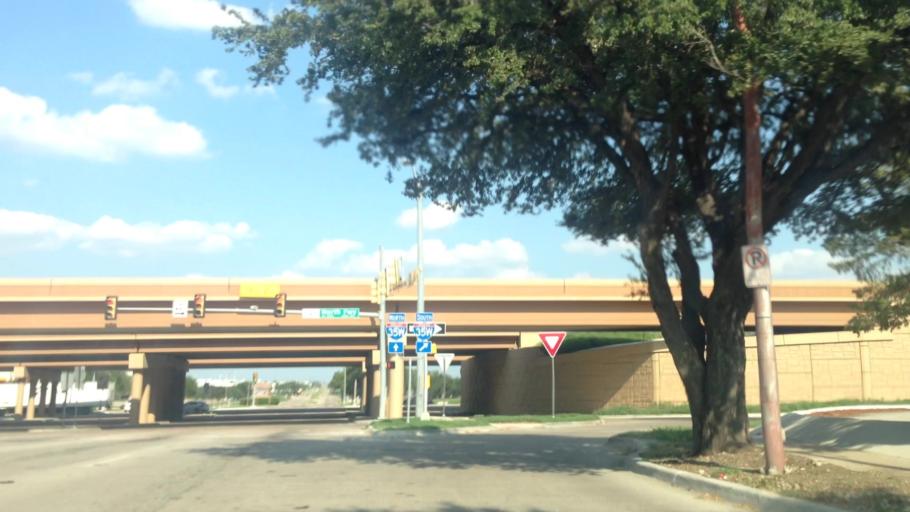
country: US
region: Texas
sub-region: Tarrant County
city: Blue Mound
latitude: 32.8242
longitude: -97.3138
